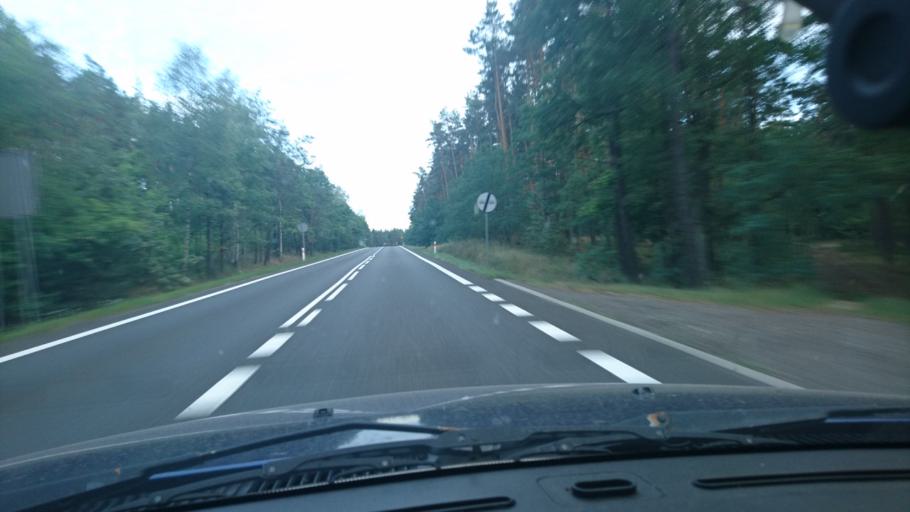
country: PL
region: Silesian Voivodeship
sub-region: Powiat lubliniecki
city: Lubliniec
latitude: 50.6014
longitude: 18.7012
